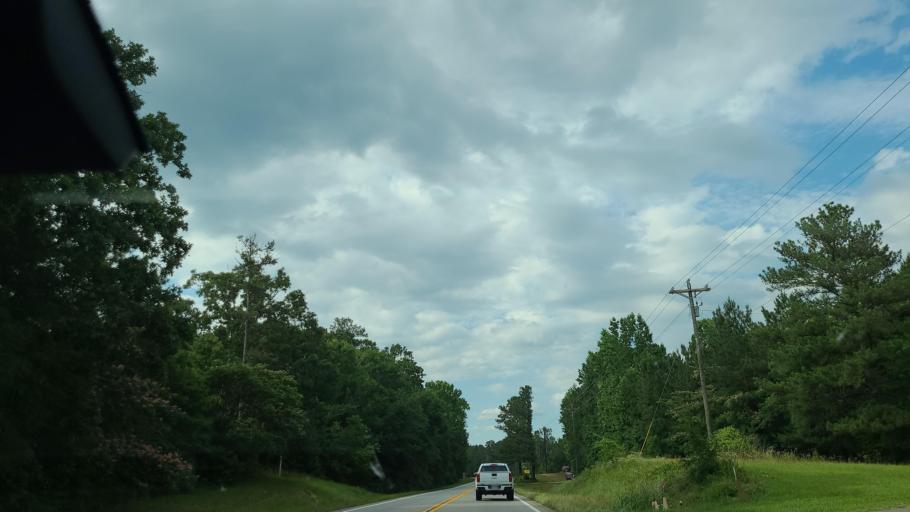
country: US
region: Georgia
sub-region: Putnam County
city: Eatonton
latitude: 33.1647
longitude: -83.4425
